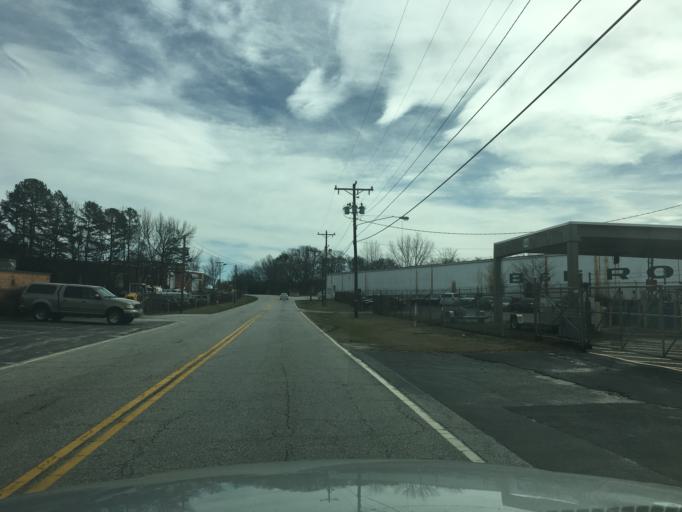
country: US
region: South Carolina
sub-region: Greenville County
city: Greenville
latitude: 34.8463
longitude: -82.3592
